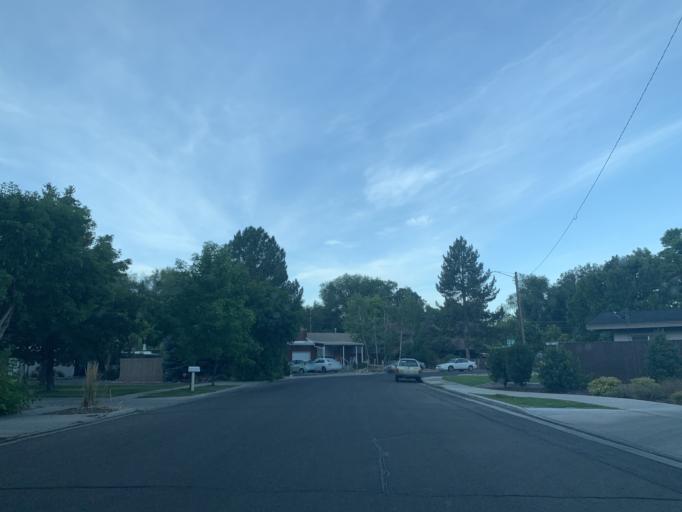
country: US
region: Utah
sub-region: Utah County
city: Provo
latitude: 40.2480
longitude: -111.6719
